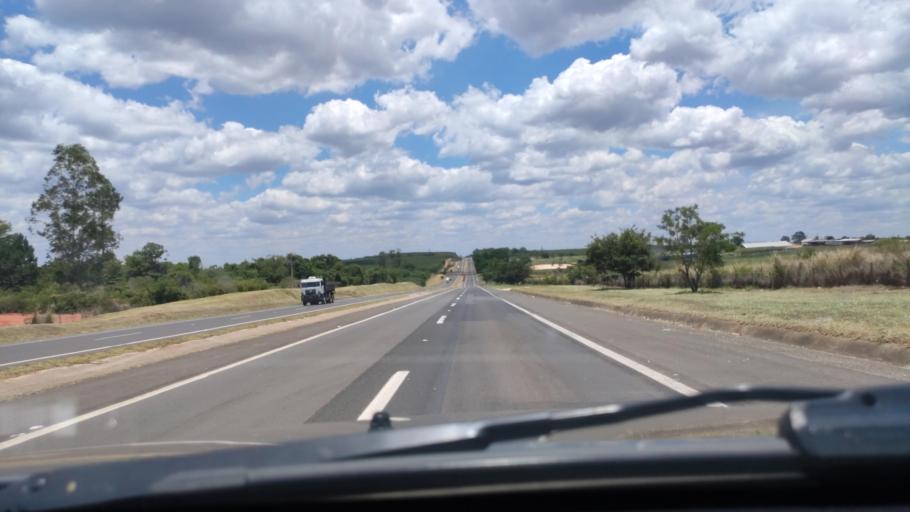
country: BR
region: Sao Paulo
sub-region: Duartina
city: Duartina
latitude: -22.5032
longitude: -49.2819
